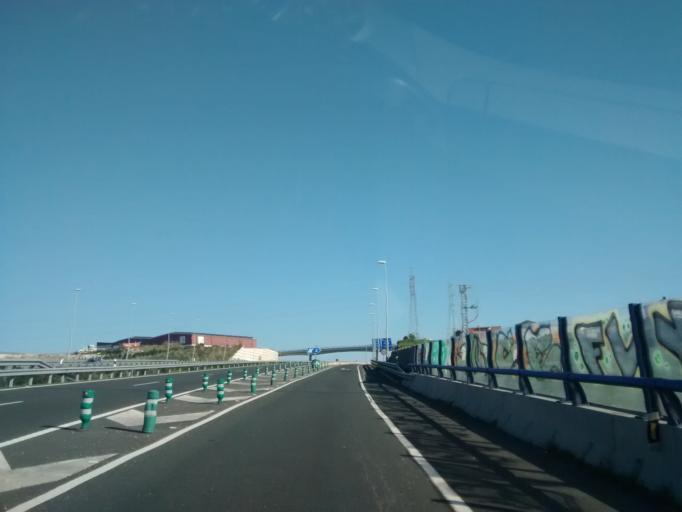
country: ES
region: Cantabria
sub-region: Provincia de Cantabria
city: Camargo
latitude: 43.4324
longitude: -3.8755
